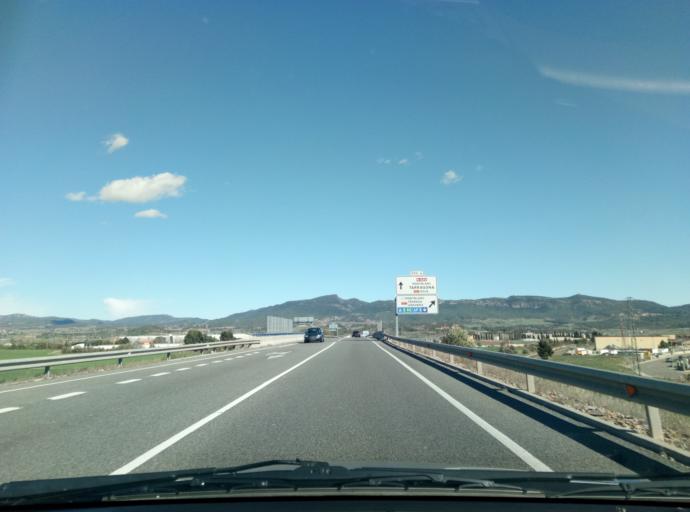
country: ES
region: Catalonia
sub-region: Provincia de Tarragona
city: Montblanc
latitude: 41.3883
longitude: 1.1558
